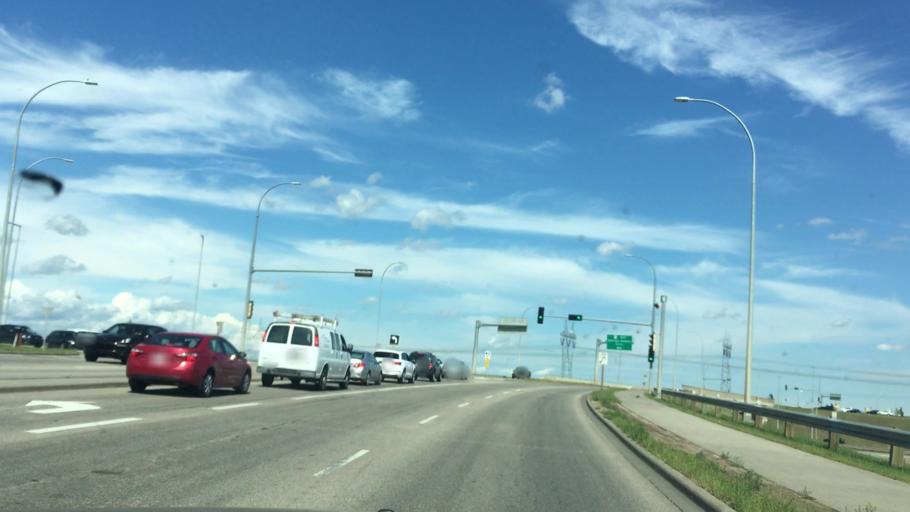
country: CA
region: Alberta
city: Edmonton
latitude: 53.4327
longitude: -113.5187
